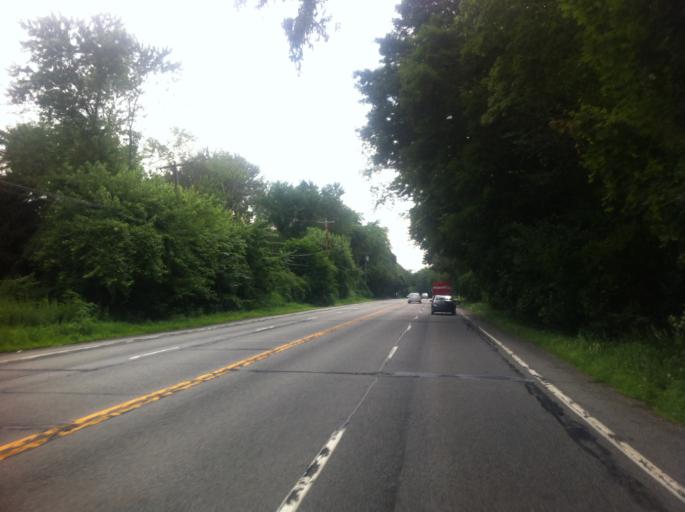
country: US
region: New York
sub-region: Nassau County
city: Upper Brookville
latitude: 40.8306
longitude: -73.5700
